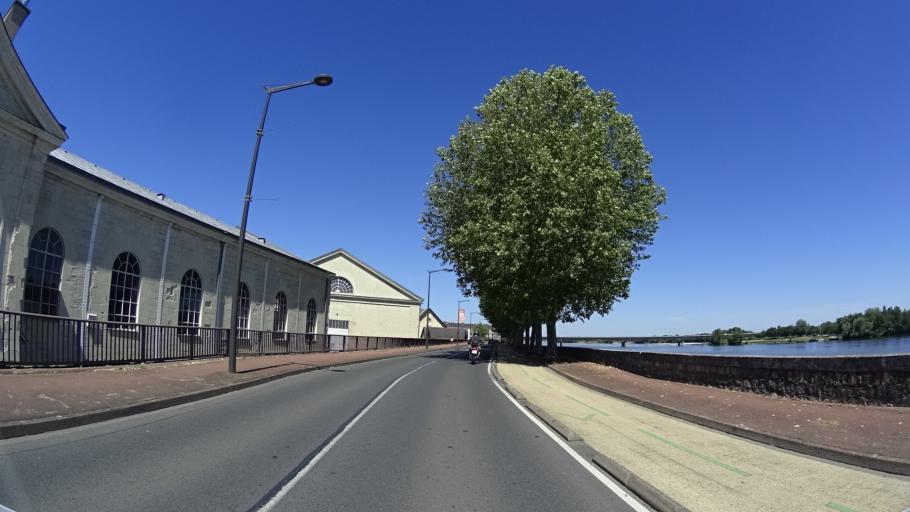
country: FR
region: Pays de la Loire
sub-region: Departement de Maine-et-Loire
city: Saumur
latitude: 47.2643
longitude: -0.0819
